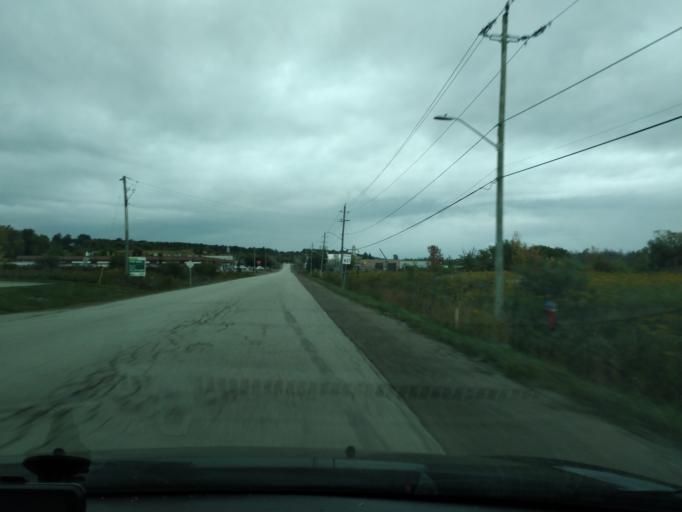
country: CA
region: Ontario
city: Bradford West Gwillimbury
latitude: 44.1338
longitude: -79.5554
